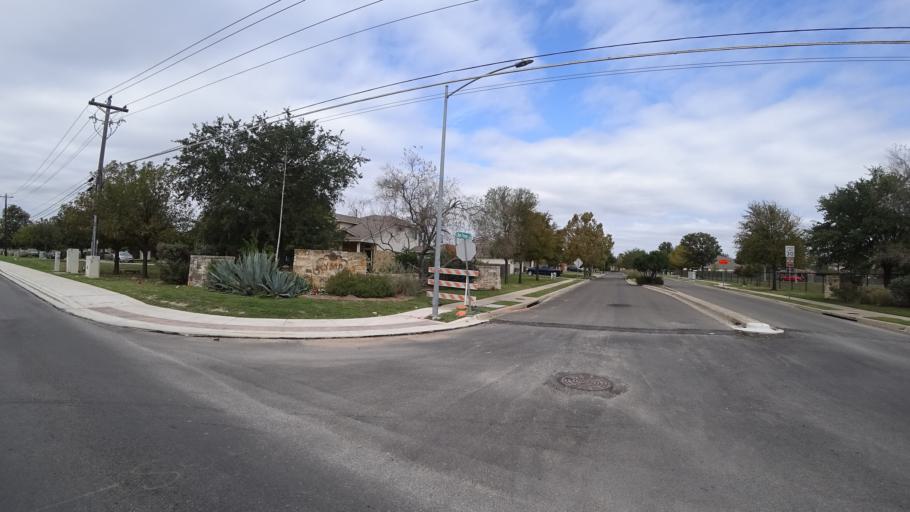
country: US
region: Texas
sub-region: Travis County
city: Manchaca
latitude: 30.1497
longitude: -97.8392
